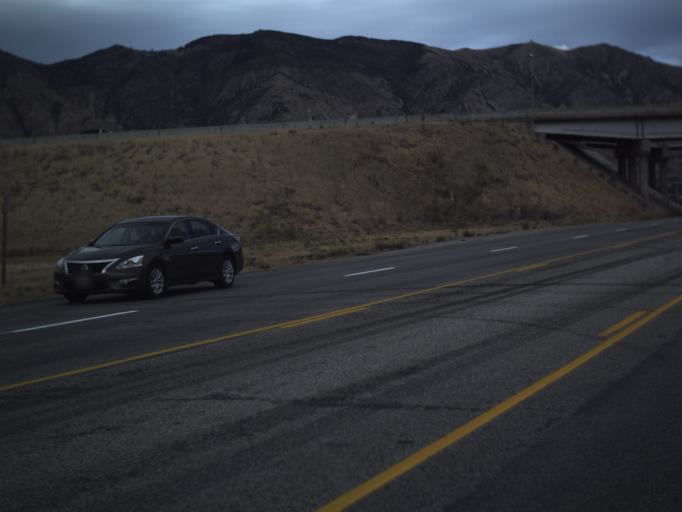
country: US
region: Utah
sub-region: Box Elder County
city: Brigham City
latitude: 41.5358
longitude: -112.0682
